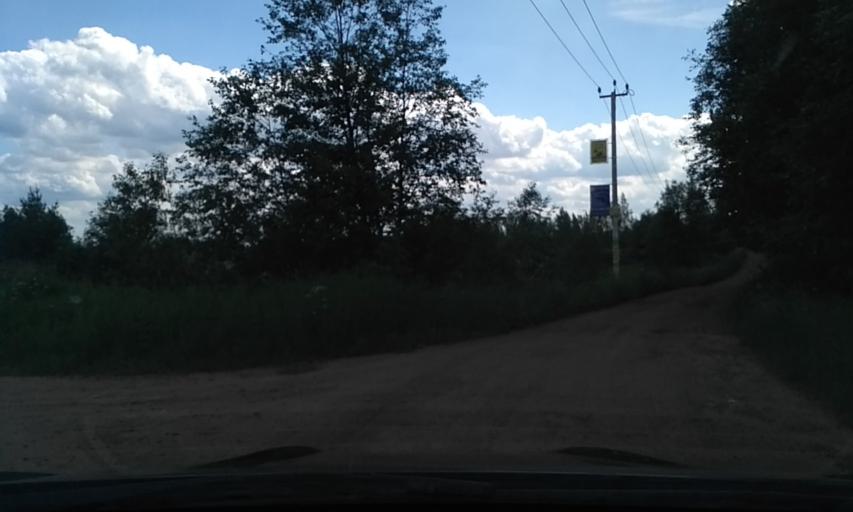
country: RU
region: Leningrad
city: Otradnoye
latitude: 59.8163
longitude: 30.8265
